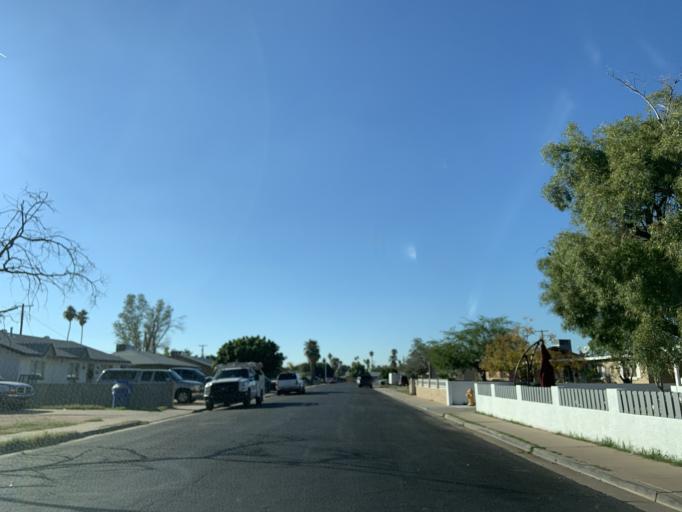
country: US
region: Arizona
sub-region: Maricopa County
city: Tempe
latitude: 33.4036
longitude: -111.8675
